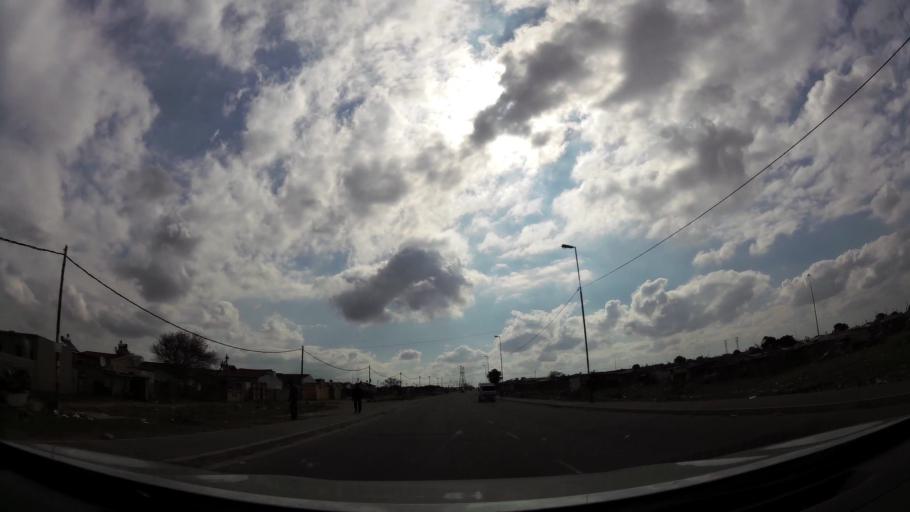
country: ZA
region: Eastern Cape
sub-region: Nelson Mandela Bay Metropolitan Municipality
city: Port Elizabeth
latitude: -33.8013
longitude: 25.5861
